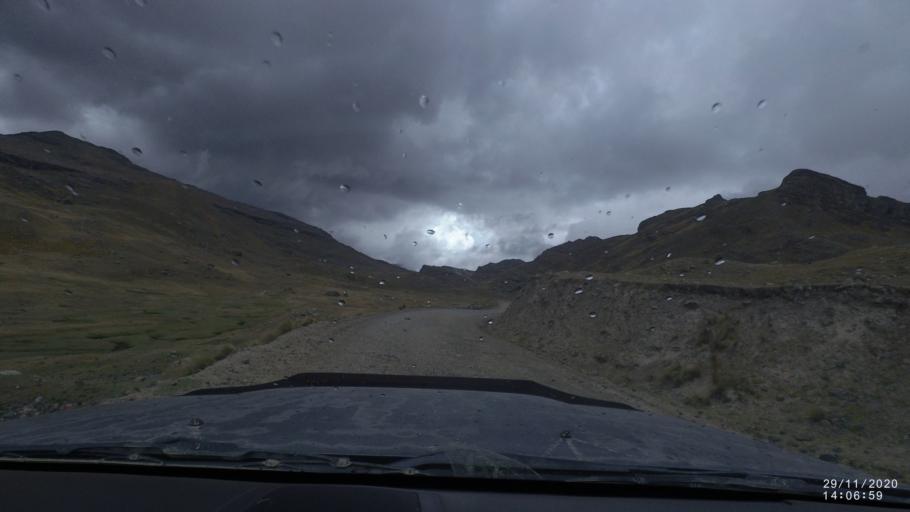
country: BO
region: Cochabamba
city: Sipe Sipe
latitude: -17.2173
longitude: -66.3810
